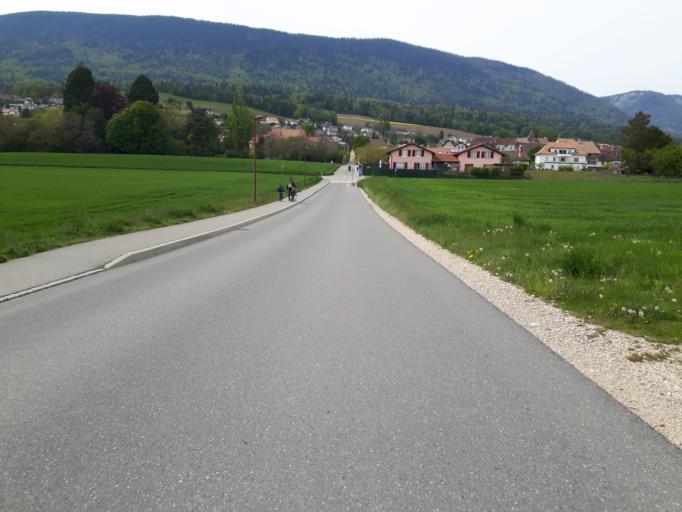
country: CH
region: Neuchatel
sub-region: Boudry District
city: Bevaix
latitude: 46.9278
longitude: 6.8181
